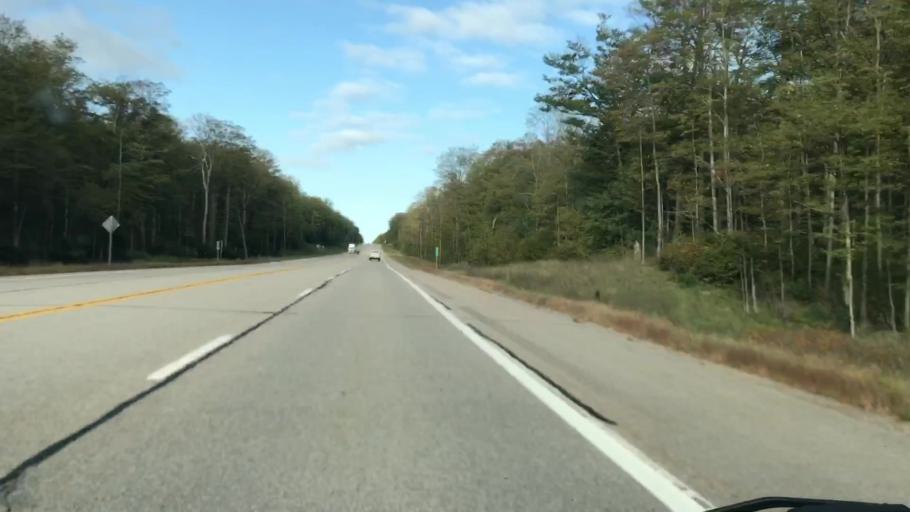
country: US
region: Michigan
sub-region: Luce County
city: Newberry
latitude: 46.3323
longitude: -85.1032
